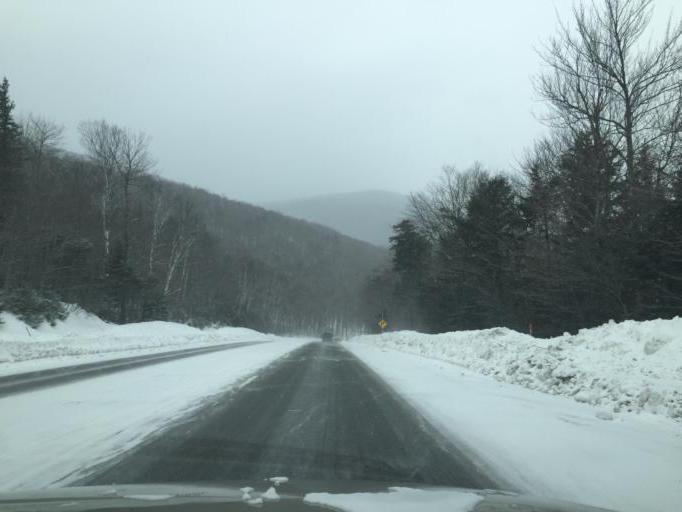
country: US
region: New Hampshire
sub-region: Coos County
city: Gorham
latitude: 44.2202
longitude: -71.2512
